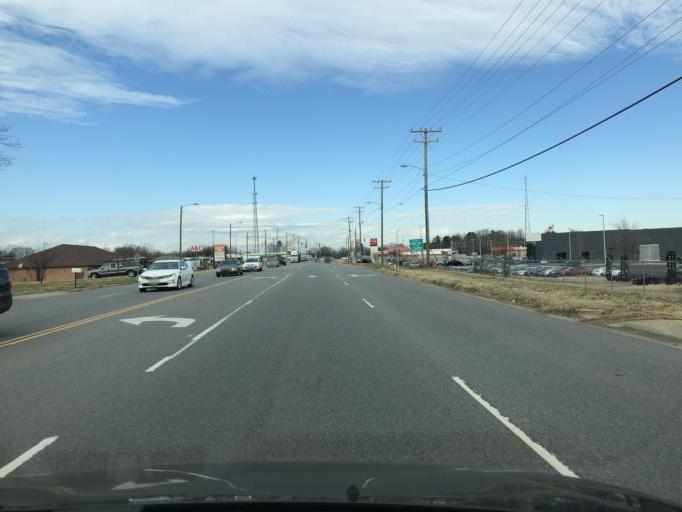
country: US
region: North Carolina
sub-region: Cleveland County
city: Shelby
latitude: 35.2688
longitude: -81.4976
